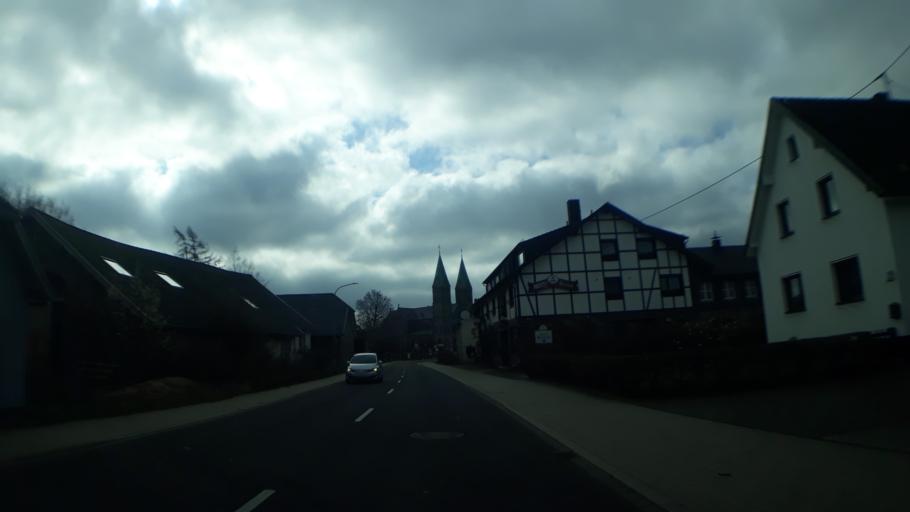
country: DE
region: North Rhine-Westphalia
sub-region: Regierungsbezirk Koln
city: Monschau
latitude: 50.5227
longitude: 6.2198
